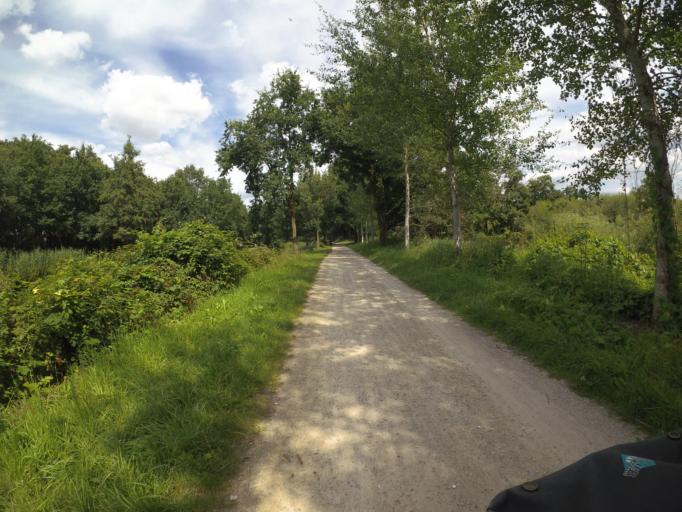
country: NL
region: North Brabant
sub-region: Gemeente Geldrop-Mierlo
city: Geldrop
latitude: 51.4341
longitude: 5.5474
